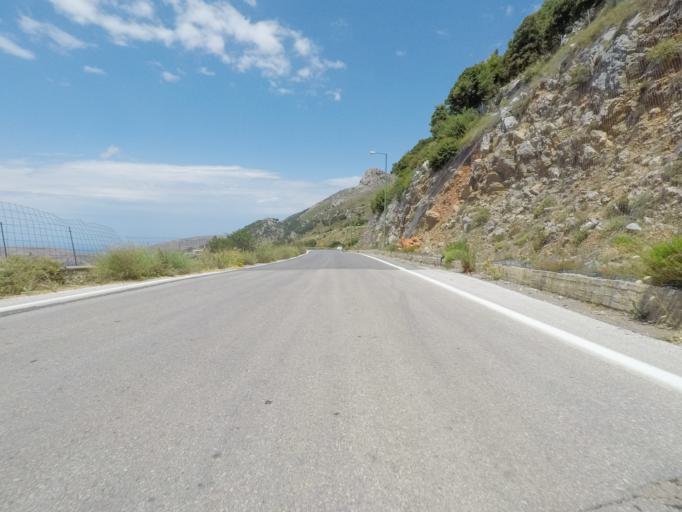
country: GR
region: Crete
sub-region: Nomos Irakleiou
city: Mokhos
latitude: 35.2076
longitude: 25.4583
